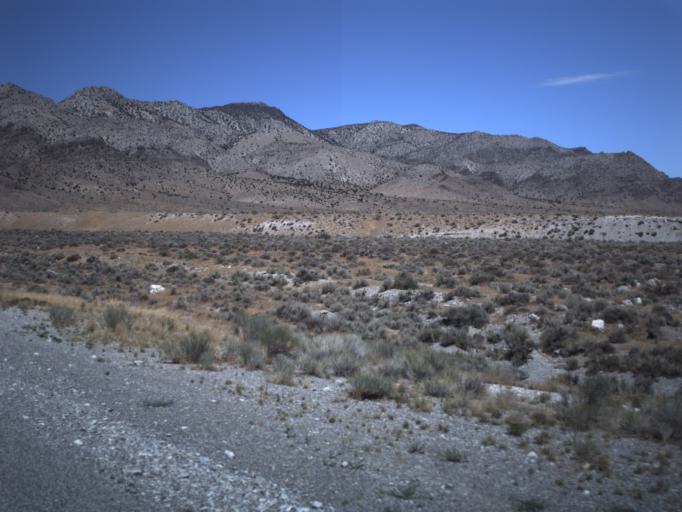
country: US
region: Utah
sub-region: Beaver County
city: Milford
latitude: 39.0875
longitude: -113.5451
